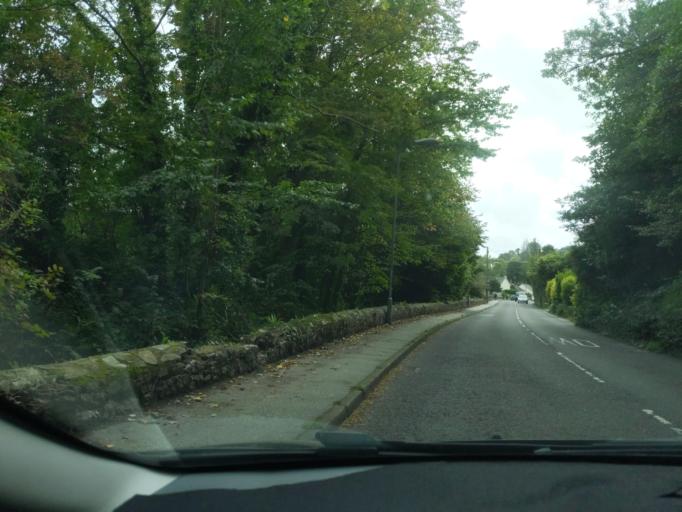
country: GB
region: England
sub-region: Cornwall
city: Par
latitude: 50.3534
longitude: -4.7107
